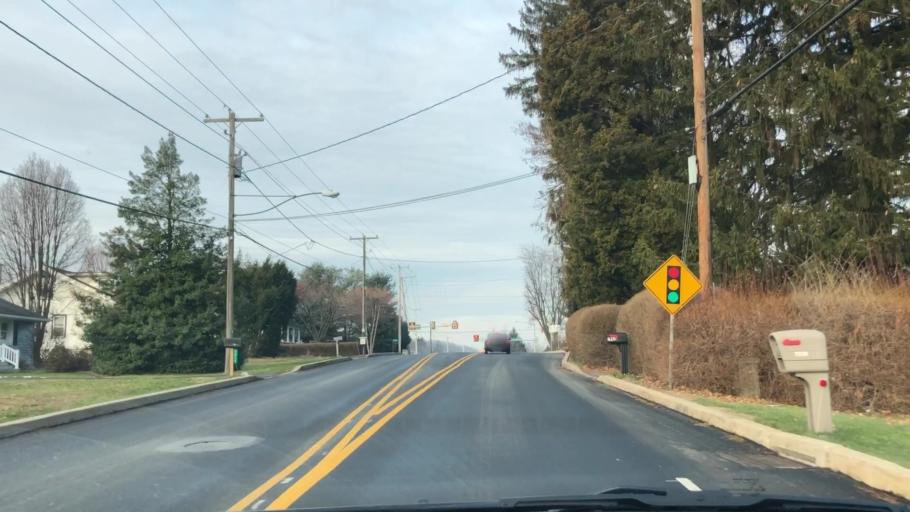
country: US
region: Pennsylvania
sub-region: Lancaster County
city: Mountville
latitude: 40.0573
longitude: -76.3967
